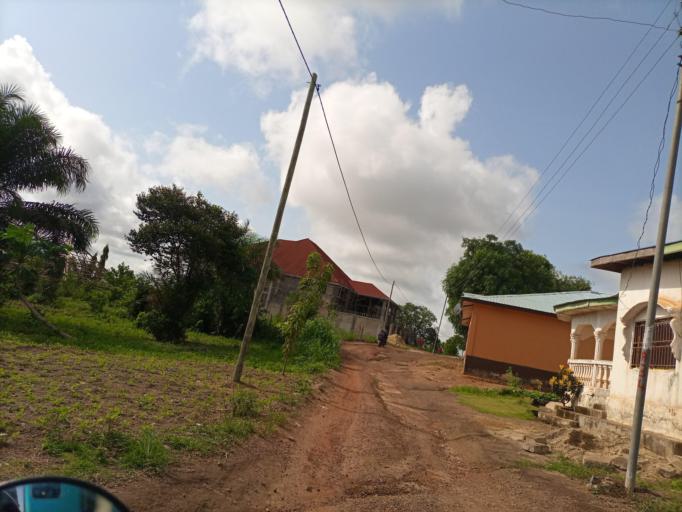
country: SL
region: Southern Province
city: Bo
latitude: 7.9613
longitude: -11.7643
